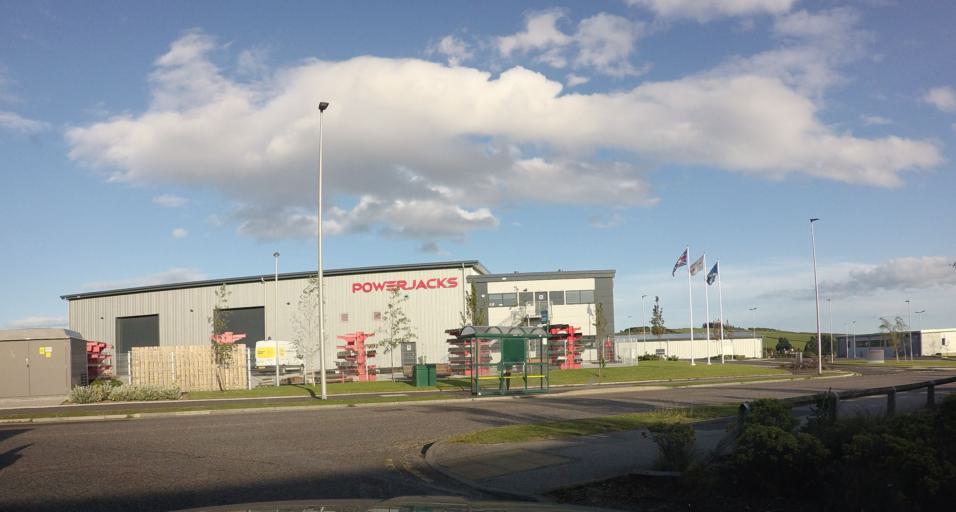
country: GB
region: Scotland
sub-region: Aberdeenshire
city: Westhill
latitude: 57.1482
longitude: -2.2728
